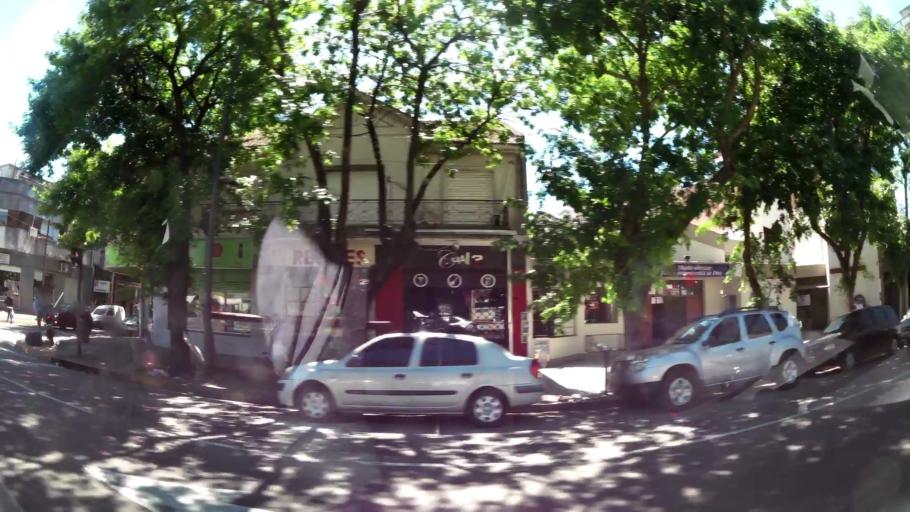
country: AR
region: Buenos Aires
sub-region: Partido de Vicente Lopez
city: Olivos
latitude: -34.5037
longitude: -58.4945
